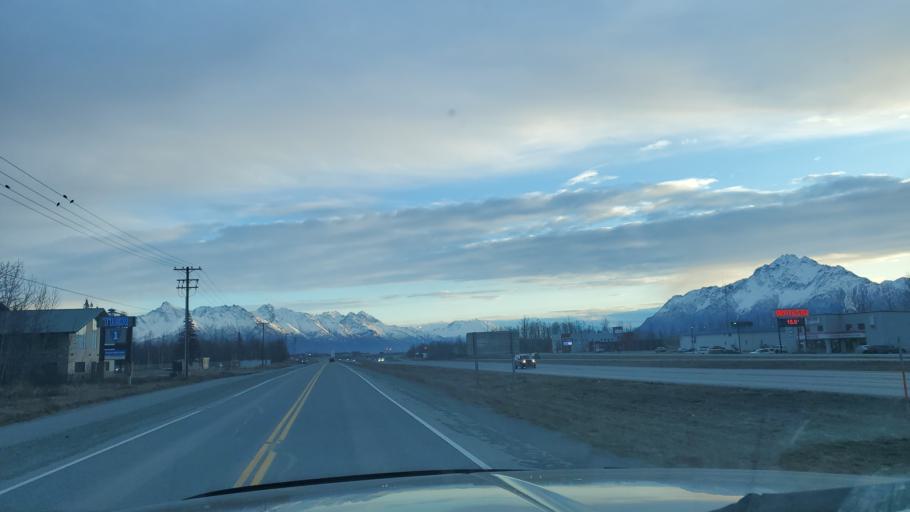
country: US
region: Alaska
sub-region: Matanuska-Susitna Borough
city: Lakes
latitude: 61.5632
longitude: -149.2917
